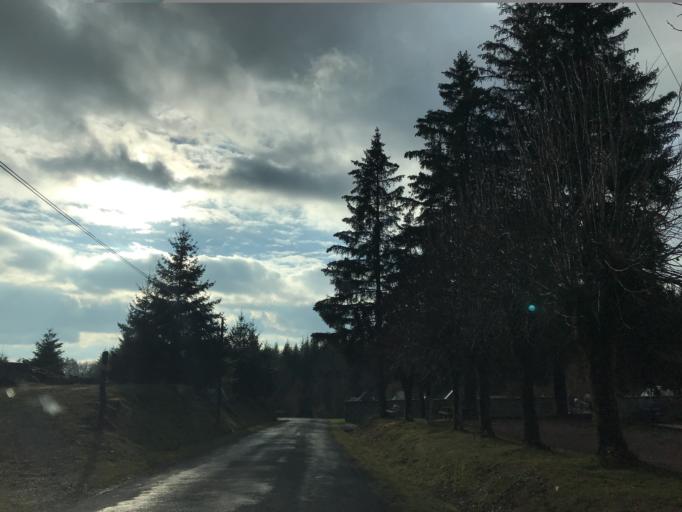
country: FR
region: Auvergne
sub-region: Departement du Puy-de-Dome
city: Celles-sur-Durolle
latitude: 45.7834
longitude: 3.6726
